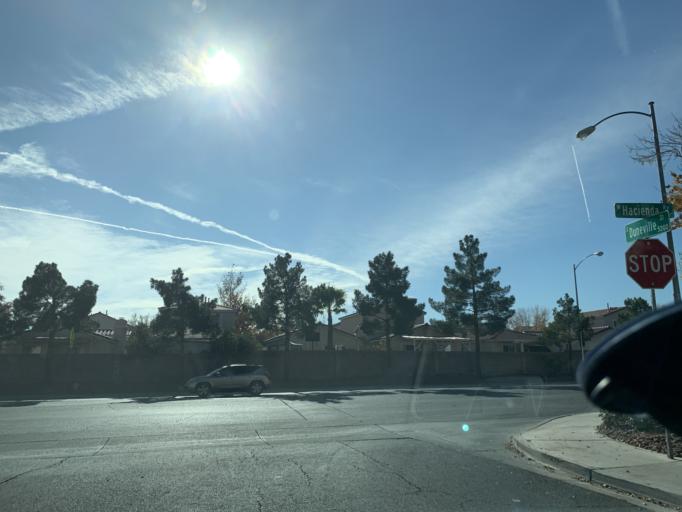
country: US
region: Nevada
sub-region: Clark County
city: Spring Valley
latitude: 36.0931
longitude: -115.2209
